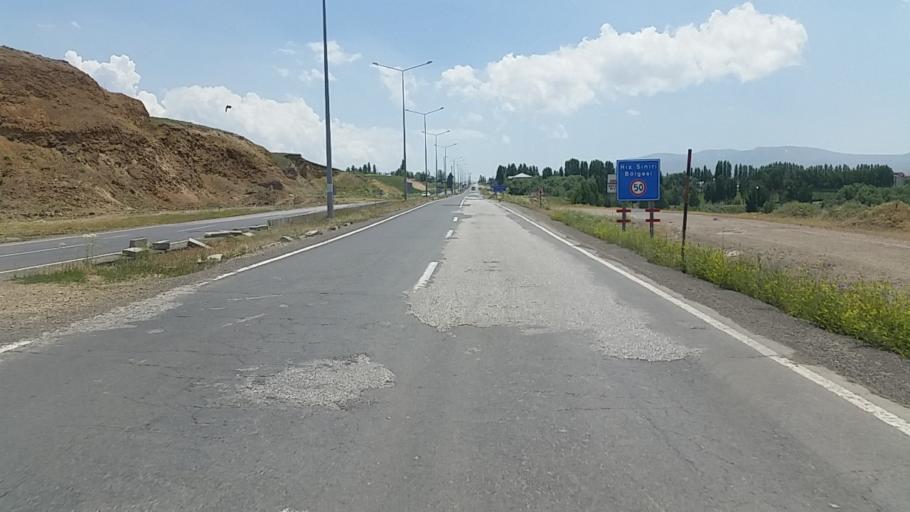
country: TR
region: Agri
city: Taslicay
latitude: 39.6476
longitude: 43.3655
